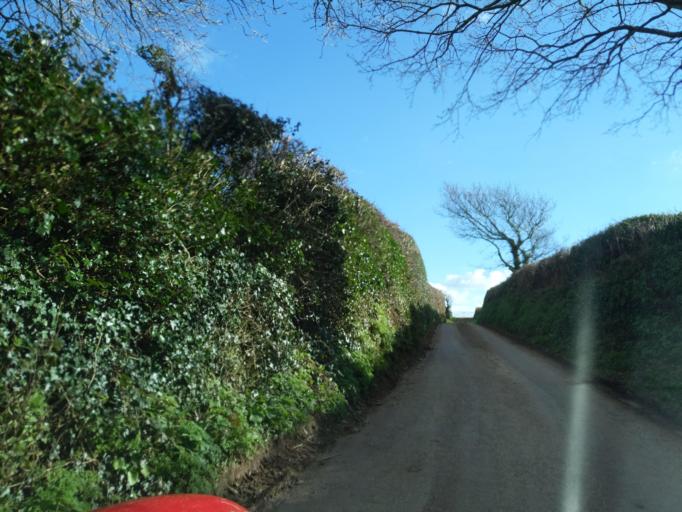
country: GB
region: England
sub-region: Devon
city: Kingsbridge
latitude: 50.2909
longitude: -3.7567
